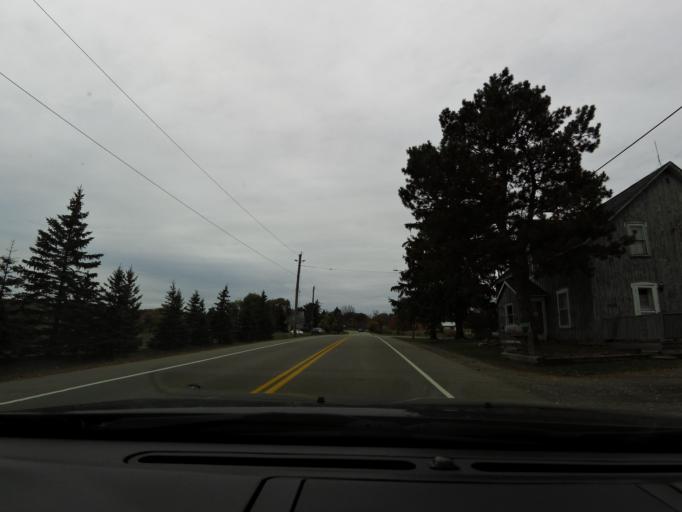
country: CA
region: Ontario
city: Hamilton
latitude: 43.3087
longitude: -79.8890
